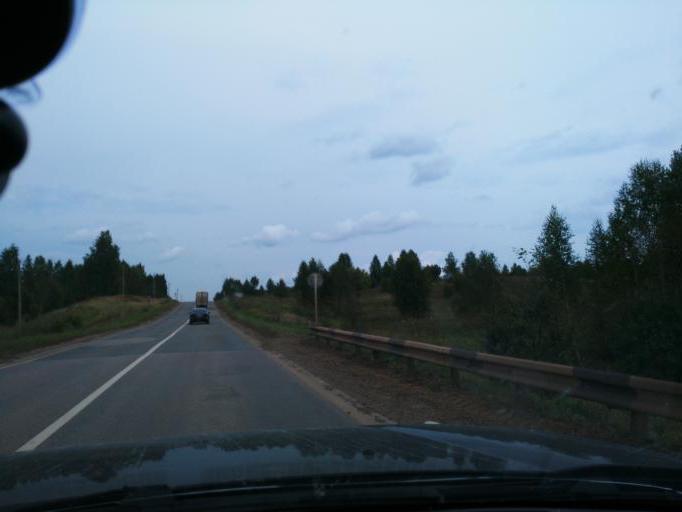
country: RU
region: Bashkortostan
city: Verkhniye Tatyshly
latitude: 56.4868
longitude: 55.8035
